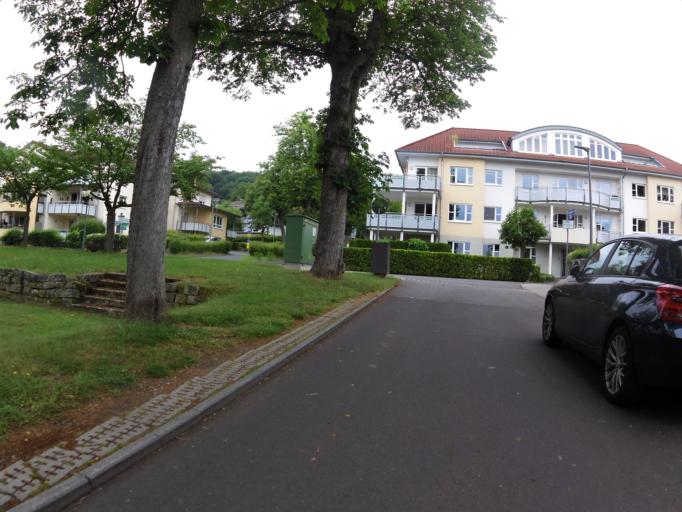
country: DE
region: Hesse
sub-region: Regierungsbezirk Kassel
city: Bad Hersfeld
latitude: 50.8635
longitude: 9.6993
